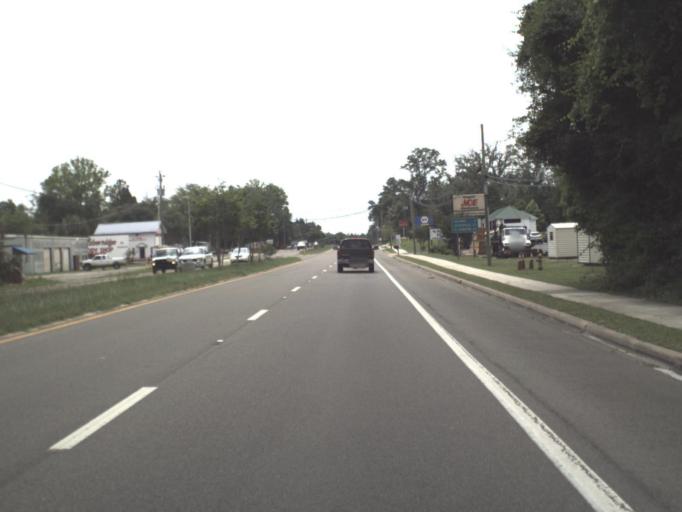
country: US
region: Florida
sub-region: Nassau County
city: Hilliard
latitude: 30.6864
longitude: -81.9147
